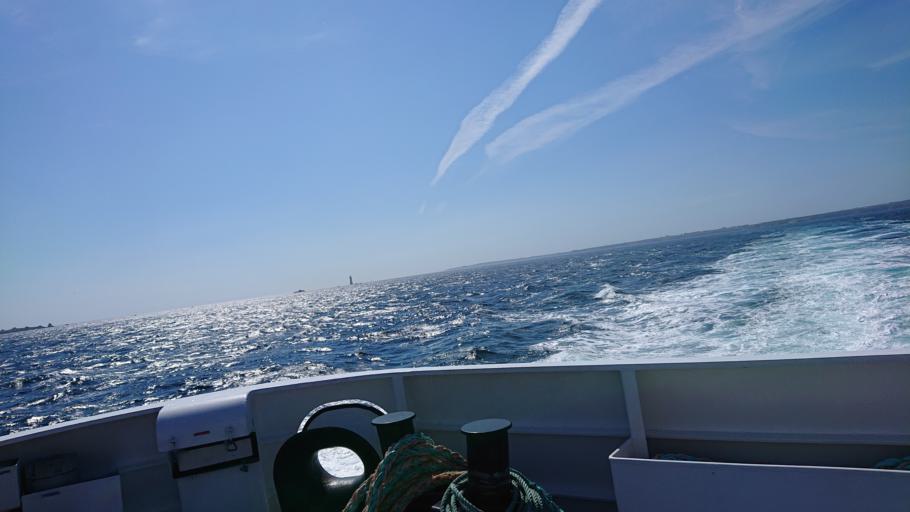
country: FR
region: Brittany
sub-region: Departement du Finistere
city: Lampaul-Plouarzel
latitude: 48.4437
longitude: -4.9886
